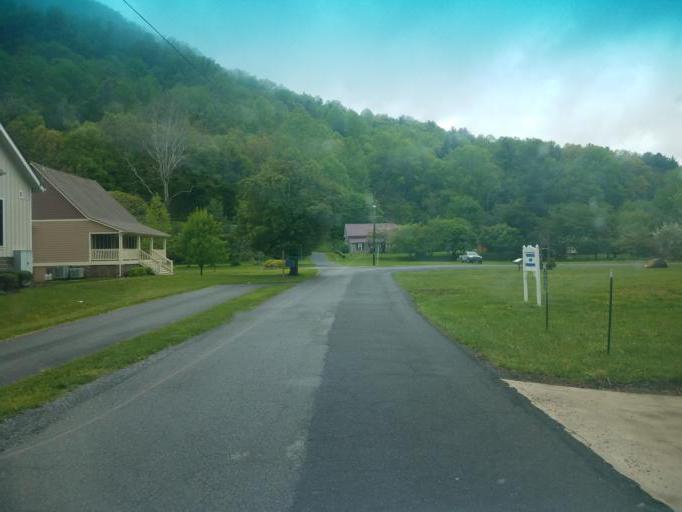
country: US
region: Virginia
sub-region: Washington County
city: Emory
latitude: 36.6315
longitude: -81.7907
